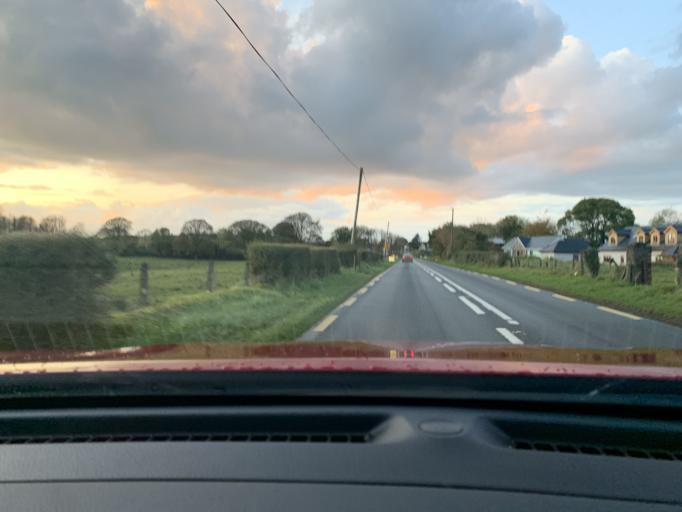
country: IE
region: Connaught
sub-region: Sligo
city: Ballymote
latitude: 54.1099
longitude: -8.4175
